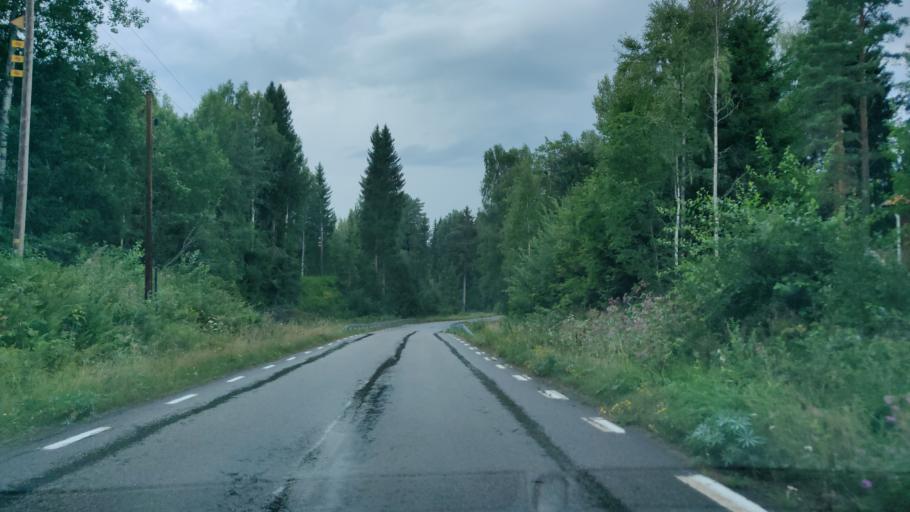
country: SE
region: Vaermland
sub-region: Munkfors Kommun
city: Munkfors
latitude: 59.8745
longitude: 13.5250
